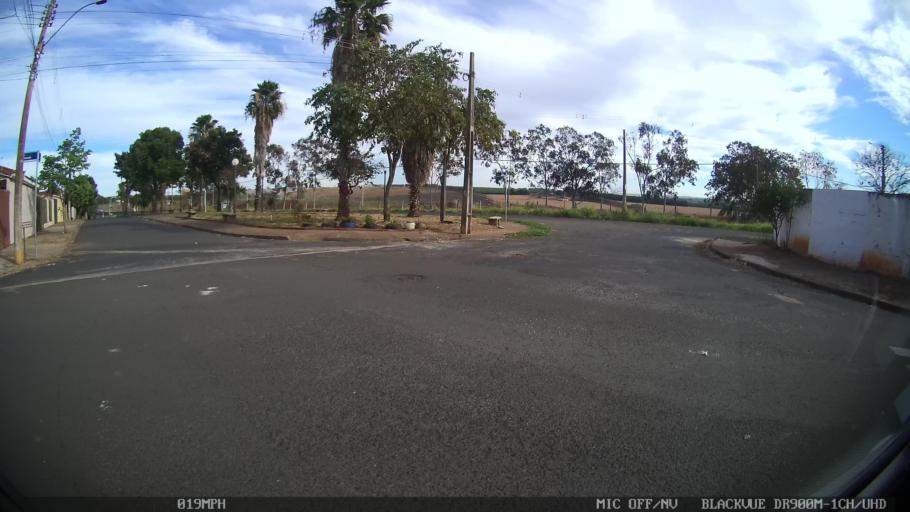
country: BR
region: Sao Paulo
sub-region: Catanduva
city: Catanduva
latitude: -21.1255
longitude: -48.9995
